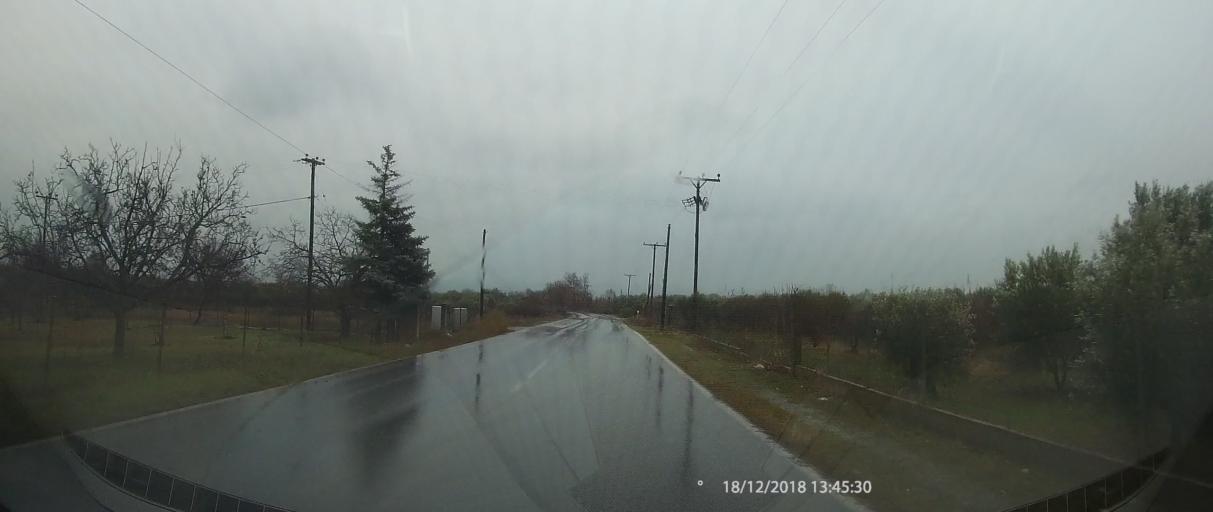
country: GR
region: Central Macedonia
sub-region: Nomos Pierias
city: Leptokarya
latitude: 40.0984
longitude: 22.5463
